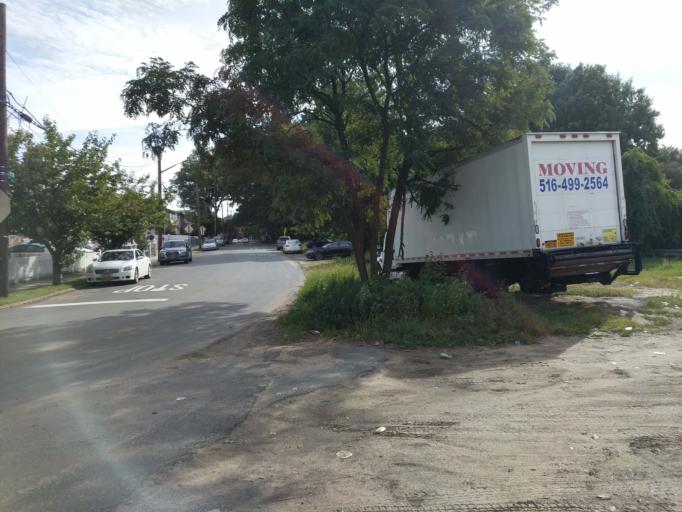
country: US
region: New York
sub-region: Queens County
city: Jamaica
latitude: 40.6794
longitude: -73.7712
